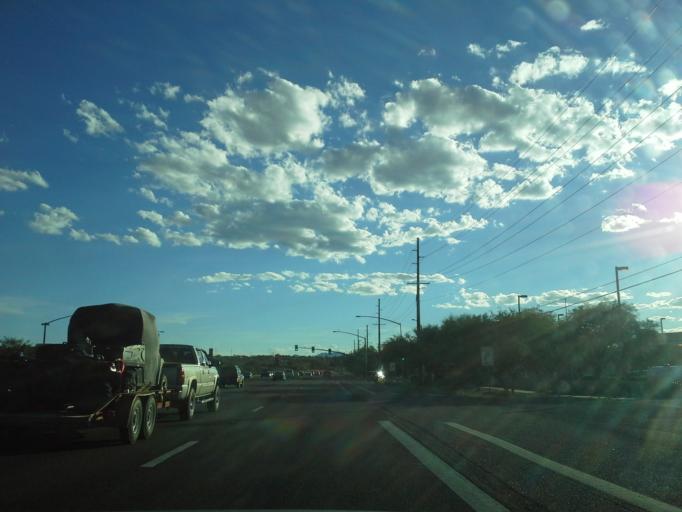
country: US
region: Arizona
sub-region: Pima County
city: Oro Valley
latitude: 32.3973
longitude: -110.9585
